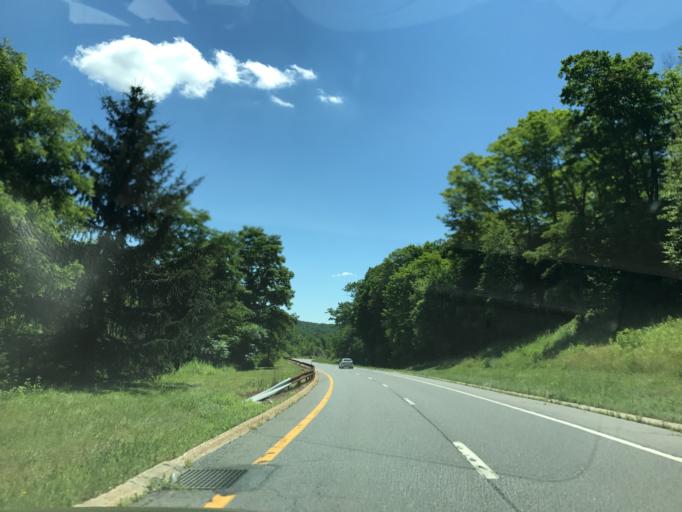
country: US
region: New York
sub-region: Putnam County
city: Mahopac
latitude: 41.4365
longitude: -73.8154
